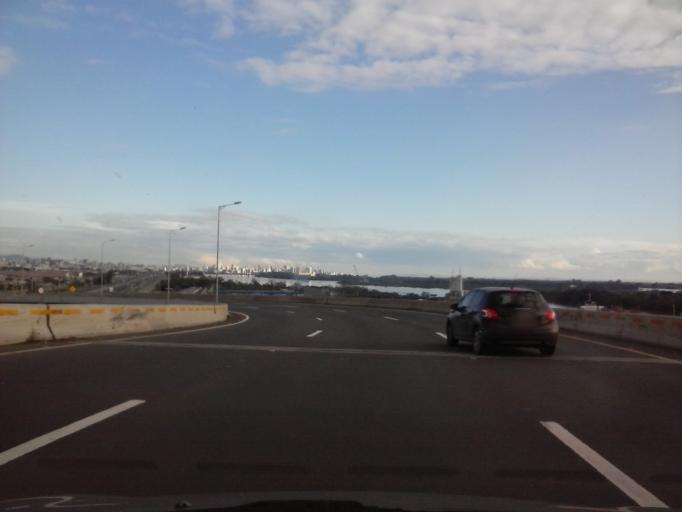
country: BR
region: Rio Grande do Sul
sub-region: Canoas
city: Canoas
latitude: -29.9734
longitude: -51.1993
